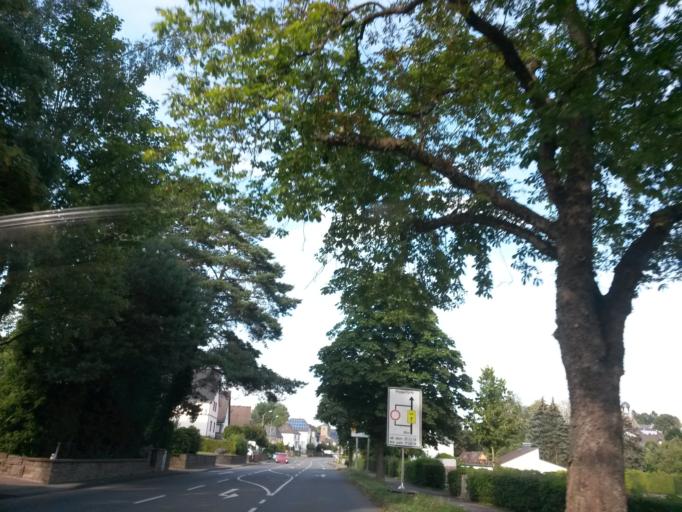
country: DE
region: North Rhine-Westphalia
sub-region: Regierungsbezirk Koln
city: Lindlar
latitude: 51.0165
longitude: 7.3684
